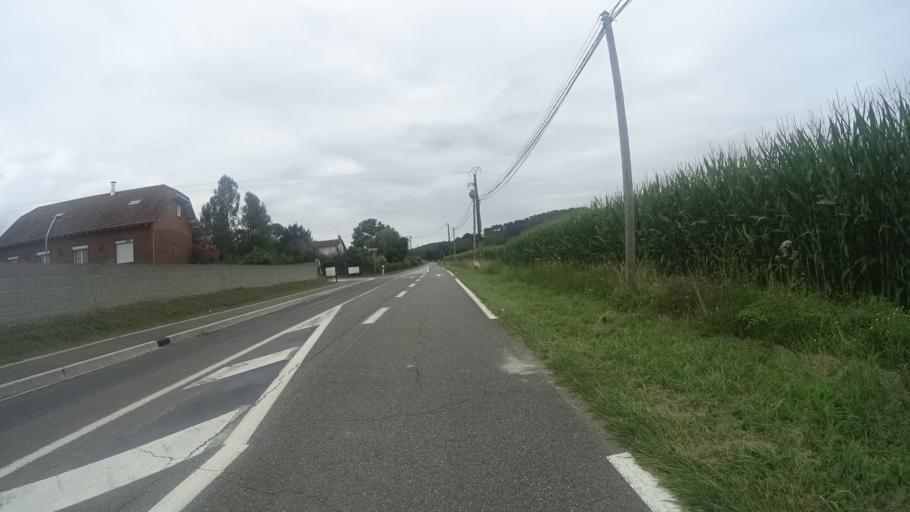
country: FR
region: Aquitaine
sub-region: Departement des Pyrenees-Atlantiques
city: Orthez
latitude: 43.4844
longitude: -0.7009
